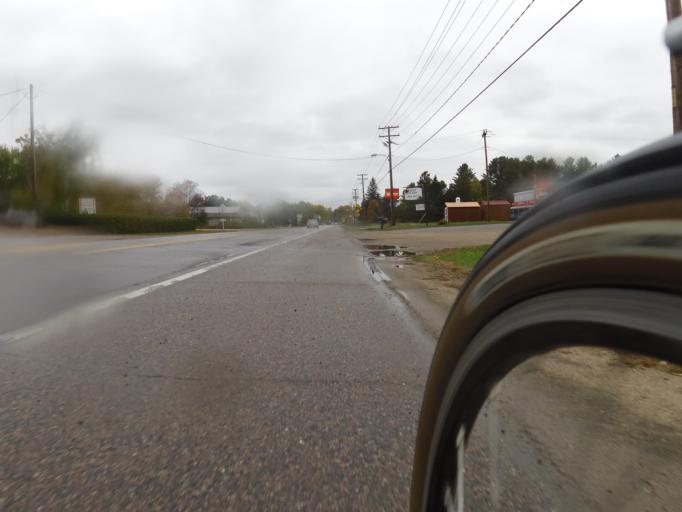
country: CA
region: Quebec
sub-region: Outaouais
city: Fort-Coulonge
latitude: 45.8532
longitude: -76.7345
